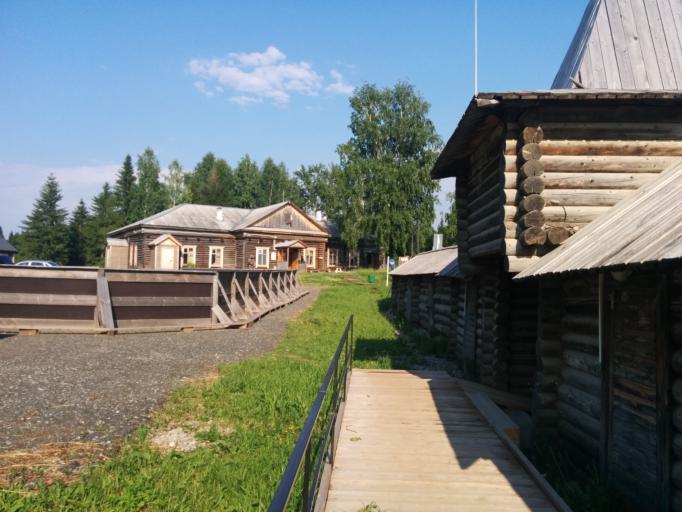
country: RU
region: Perm
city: Polazna
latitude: 58.2584
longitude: 56.2607
